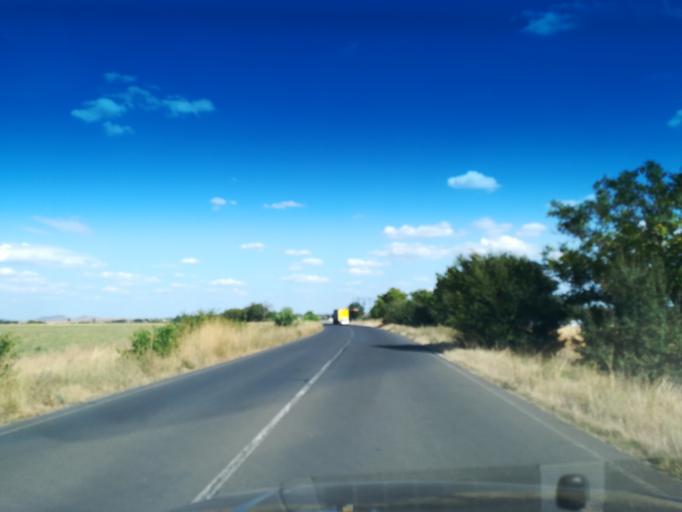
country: BG
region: Stara Zagora
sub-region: Obshtina Chirpan
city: Chirpan
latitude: 42.0590
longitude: 25.2486
